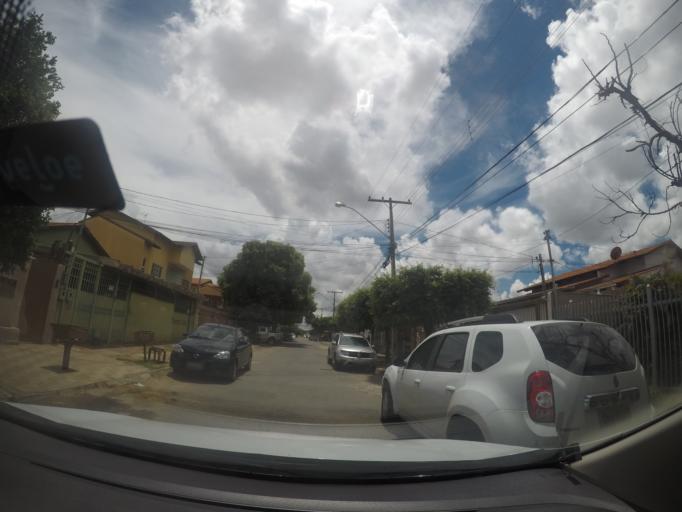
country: BR
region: Goias
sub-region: Goiania
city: Goiania
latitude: -16.6747
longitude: -49.3084
